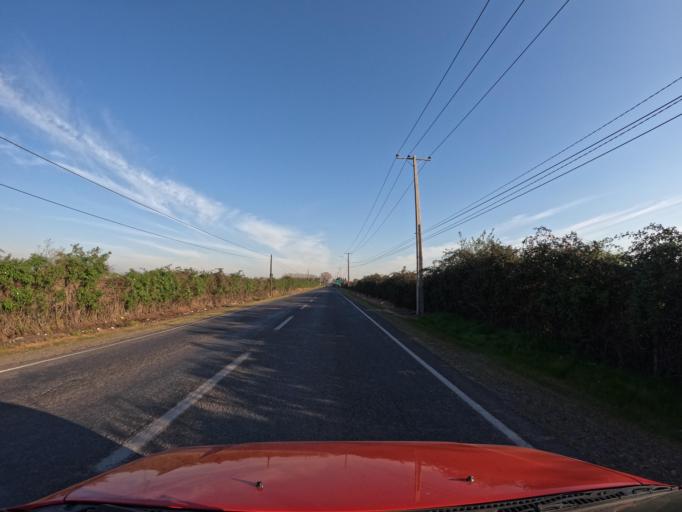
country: CL
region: Maule
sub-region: Provincia de Curico
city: Rauco
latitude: -34.9255
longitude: -71.2768
